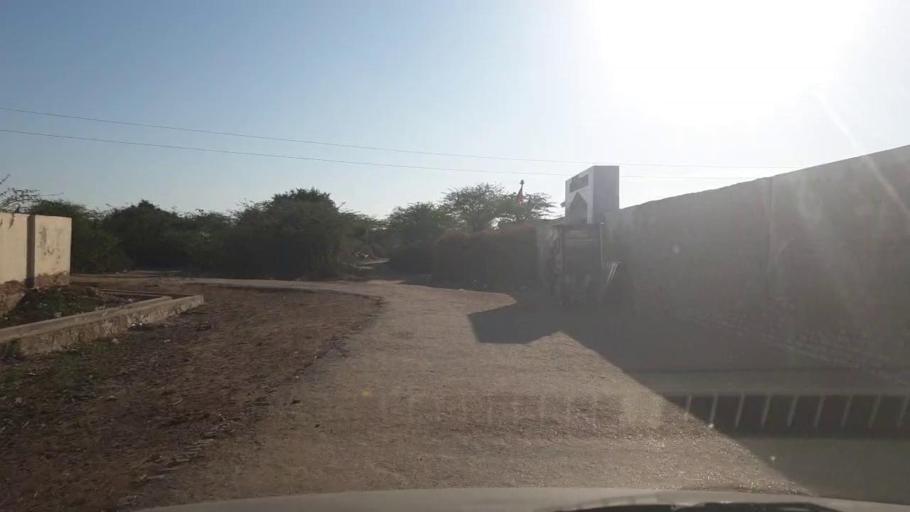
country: PK
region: Sindh
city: Dhoro Naro
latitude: 25.4336
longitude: 69.5307
